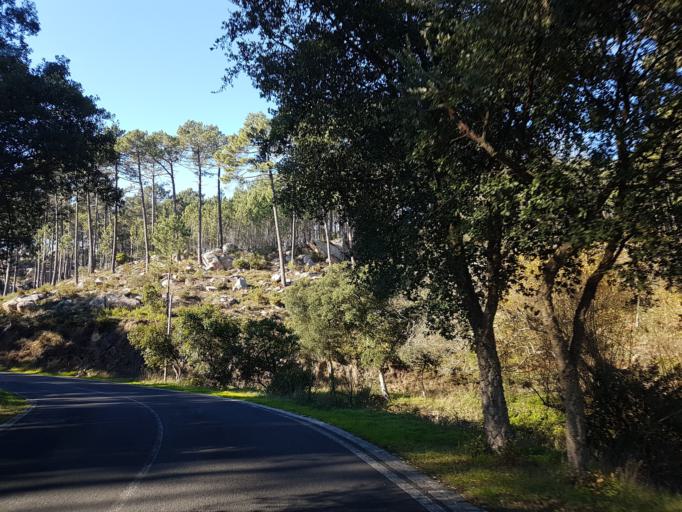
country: PT
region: Lisbon
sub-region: Cascais
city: Alcabideche
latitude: 38.7575
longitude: -9.4251
